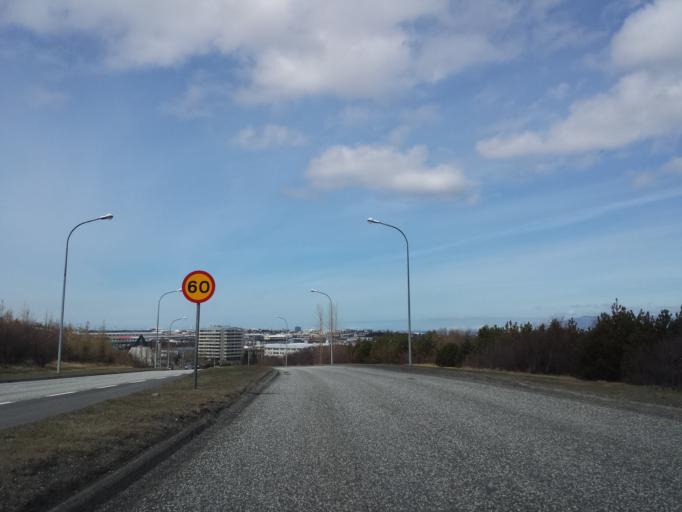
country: IS
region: Capital Region
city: Reykjavik
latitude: 64.1045
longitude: -21.8359
